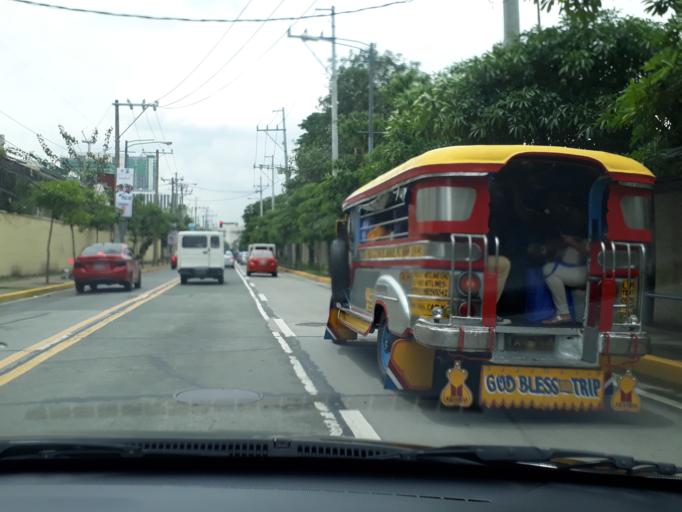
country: PH
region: Metro Manila
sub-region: Makati City
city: Makati City
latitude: 14.5649
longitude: 121.0164
